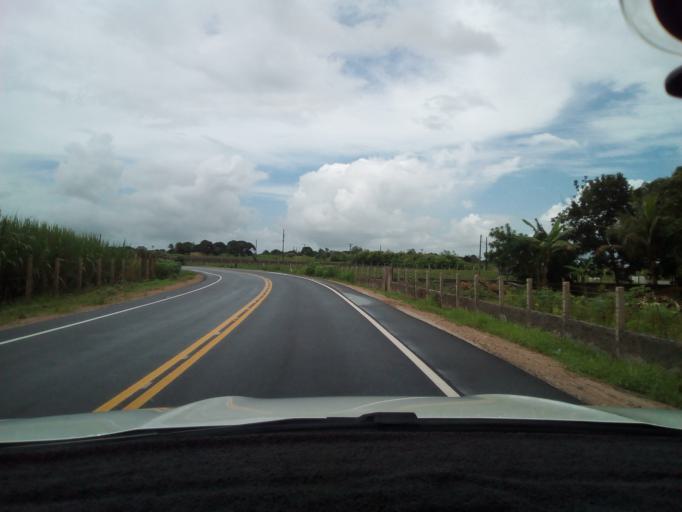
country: BR
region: Paraiba
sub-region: Pedras De Fogo
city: Pedras de Fogo
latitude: -7.3961
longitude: -35.1388
